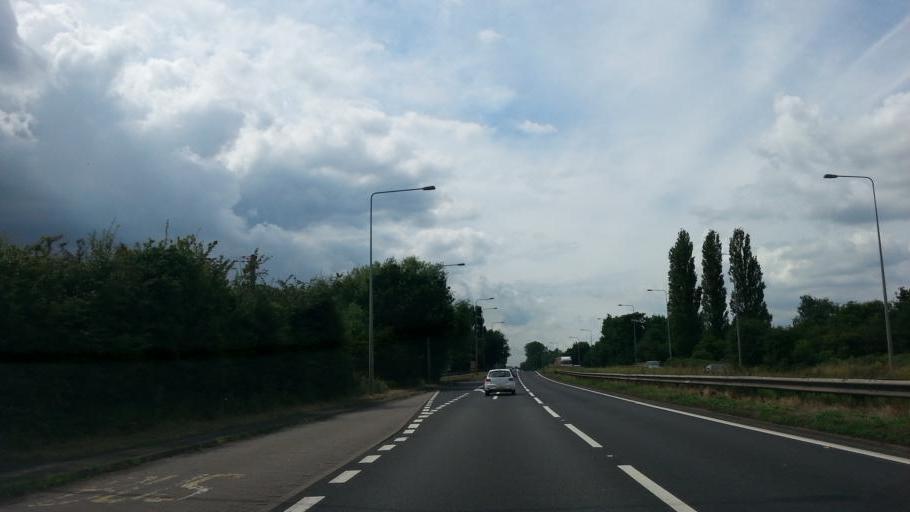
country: GB
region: England
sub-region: Staffordshire
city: Alrewas
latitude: 52.7122
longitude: -1.7646
